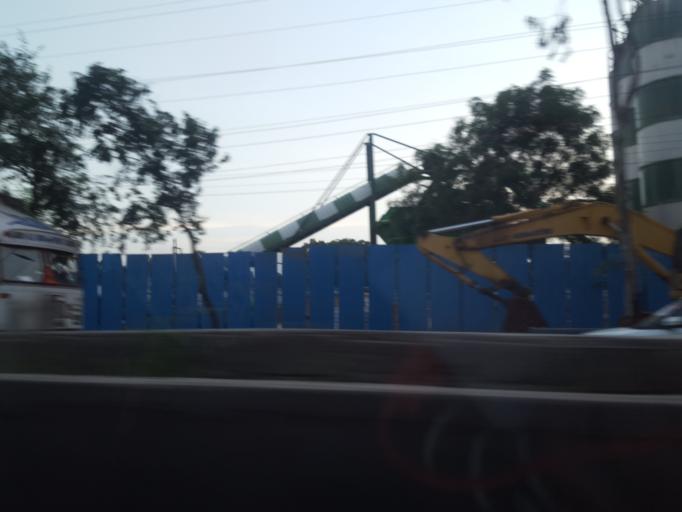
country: IN
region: Telangana
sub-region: Medak
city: Serilingampalle
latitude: 17.5238
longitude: 78.3559
